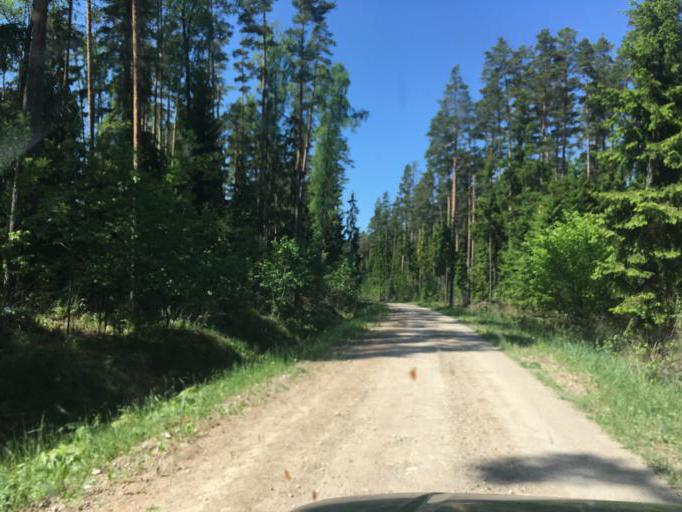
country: LV
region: Talsu Rajons
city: Valdemarpils
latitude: 57.4396
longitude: 22.6744
